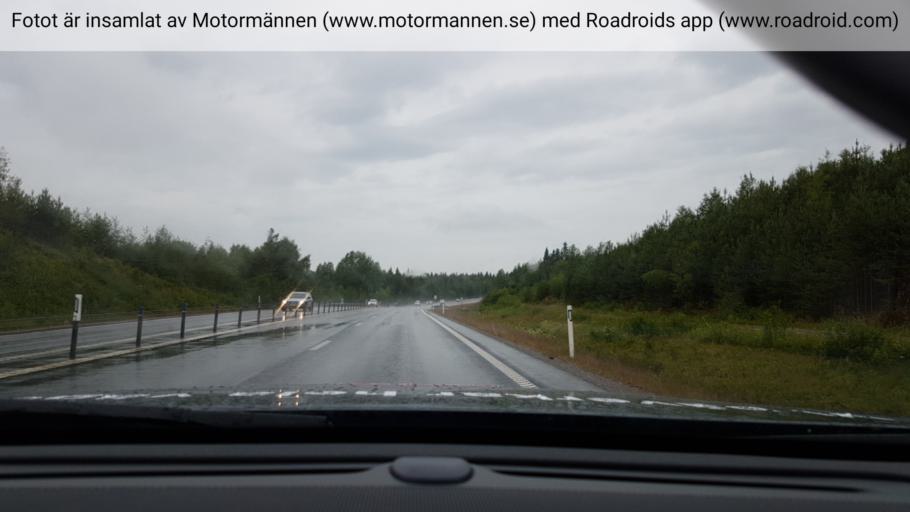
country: SE
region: Vaesterbotten
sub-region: Vannas Kommun
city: Vannasby
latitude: 63.8993
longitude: 19.9065
